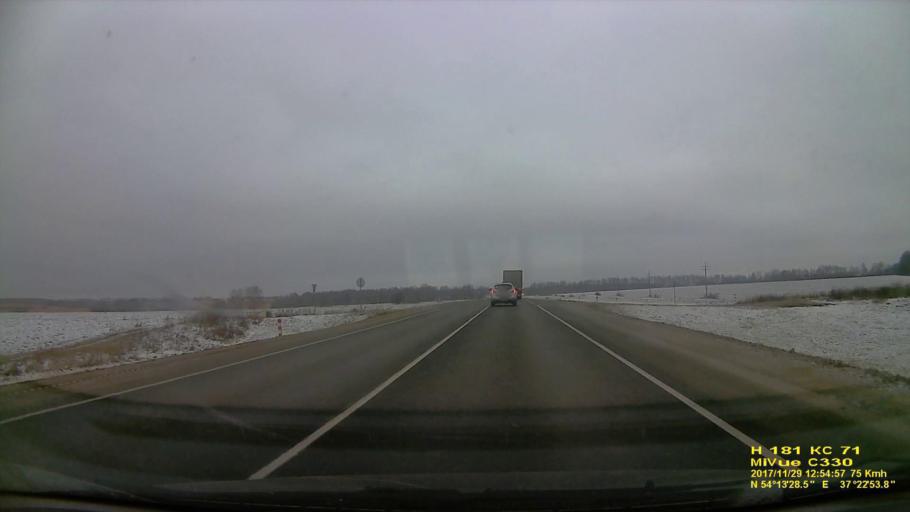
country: RU
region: Tula
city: Leninskiy
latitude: 54.2246
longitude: 37.3814
